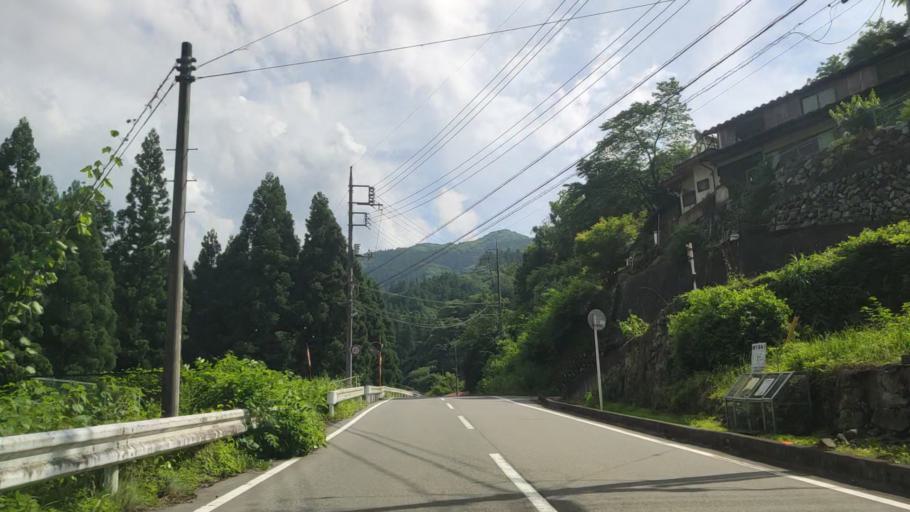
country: JP
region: Gunma
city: Tomioka
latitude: 36.1576
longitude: 138.7287
